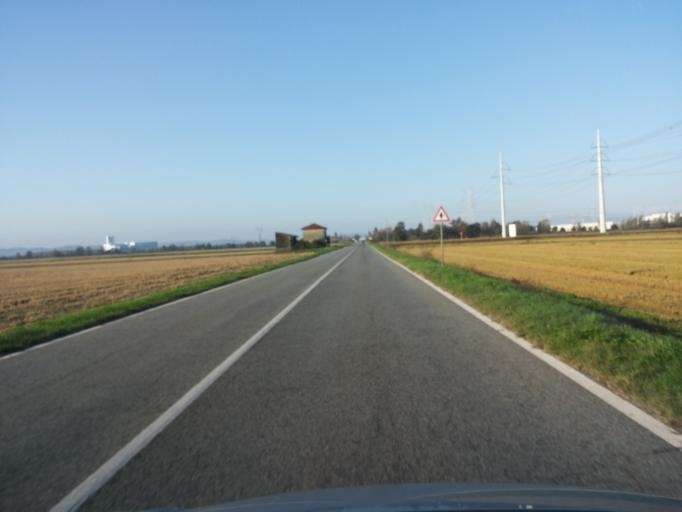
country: IT
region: Piedmont
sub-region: Provincia di Vercelli
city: Fontanetto Po
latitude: 45.2519
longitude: 8.2110
